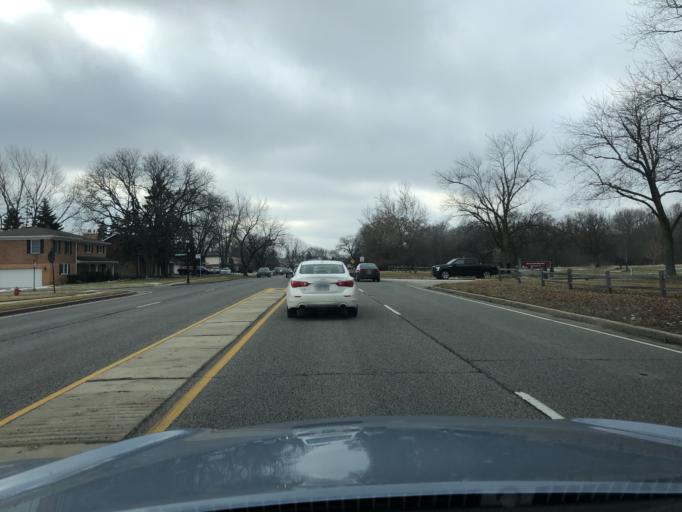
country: US
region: Illinois
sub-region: Cook County
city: Elk Grove Village
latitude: 42.0162
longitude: -87.9931
